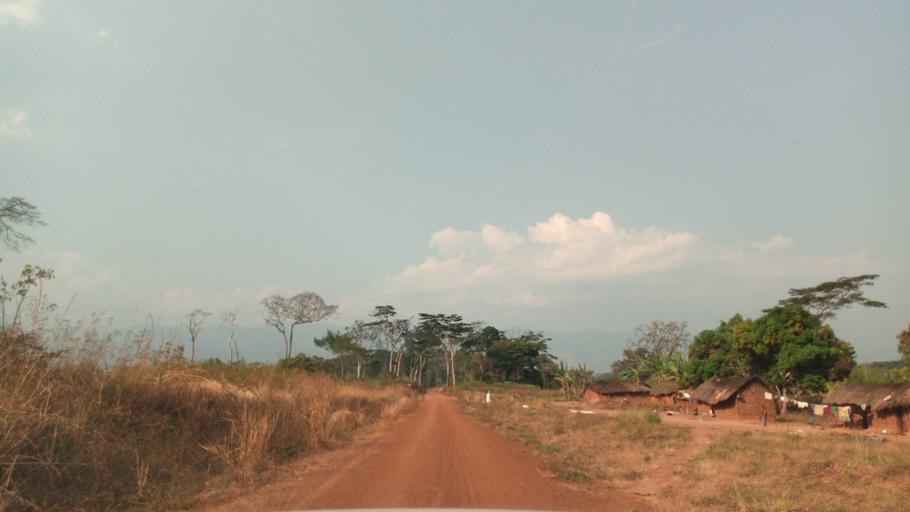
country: CD
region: Katanga
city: Kalemie
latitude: -5.2011
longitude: 28.8772
